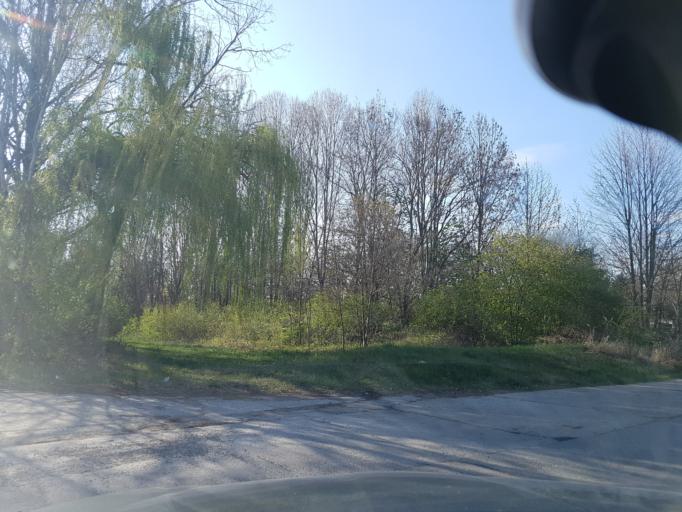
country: DE
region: Brandenburg
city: Doberlug-Kirchhain
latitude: 51.6336
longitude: 13.5551
